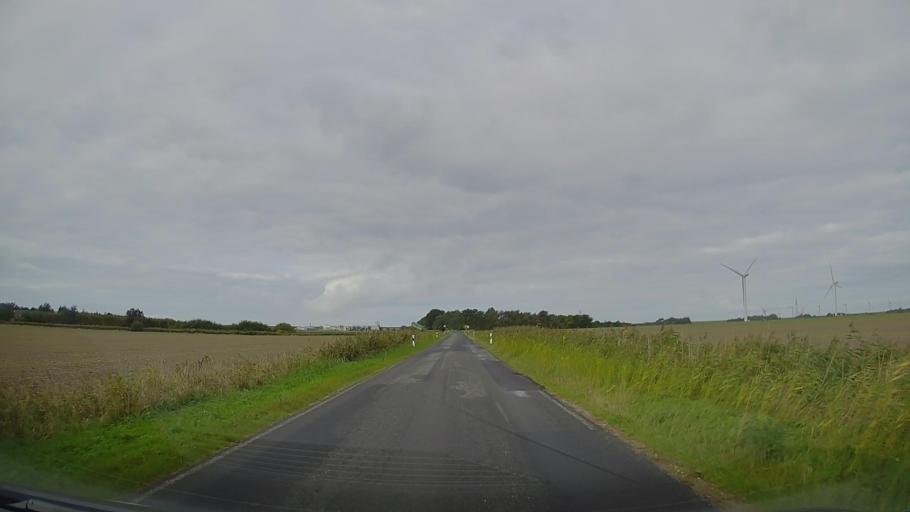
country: DE
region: Schleswig-Holstein
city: Emmelsbull-Horsbull
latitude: 54.8066
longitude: 8.6706
